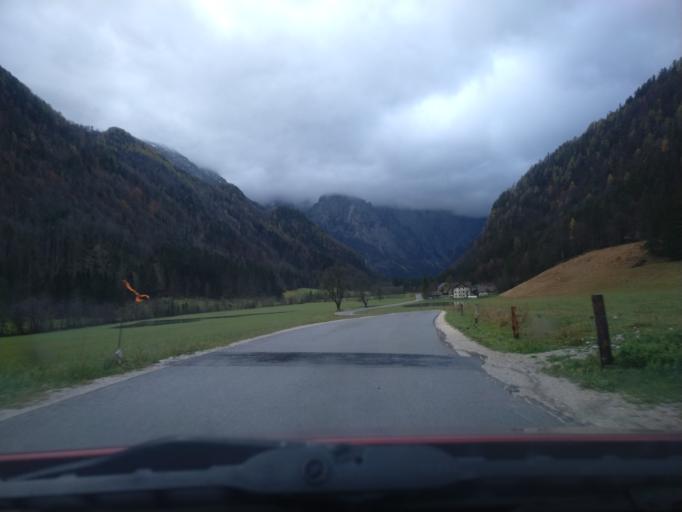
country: SI
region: Solcava
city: Solcava
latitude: 46.4180
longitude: 14.6413
